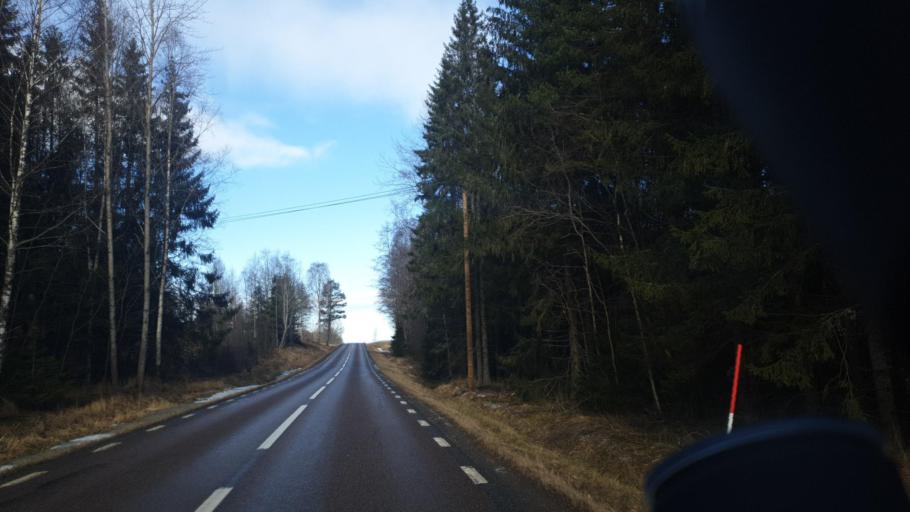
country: SE
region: Vaermland
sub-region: Arvika Kommun
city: Arvika
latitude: 59.5971
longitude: 12.5368
